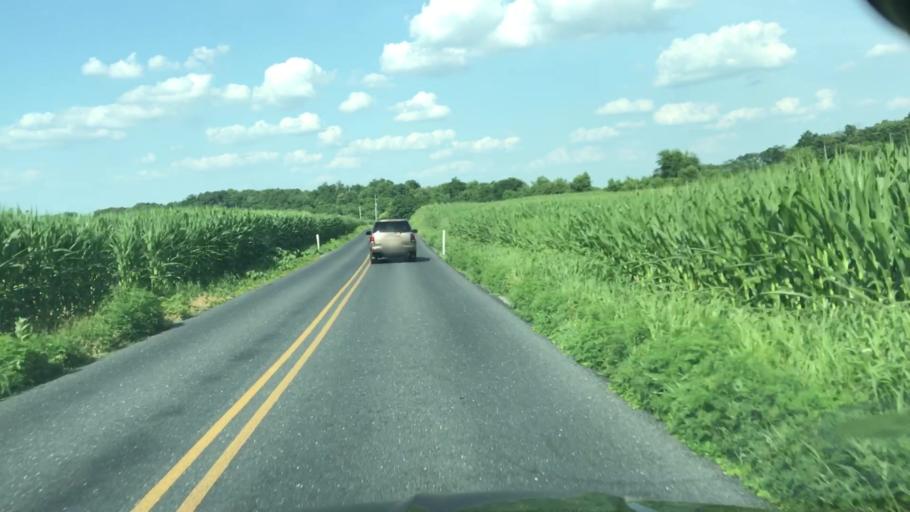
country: US
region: Pennsylvania
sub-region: Cumberland County
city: Boiling Springs
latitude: 40.1814
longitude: -77.1173
